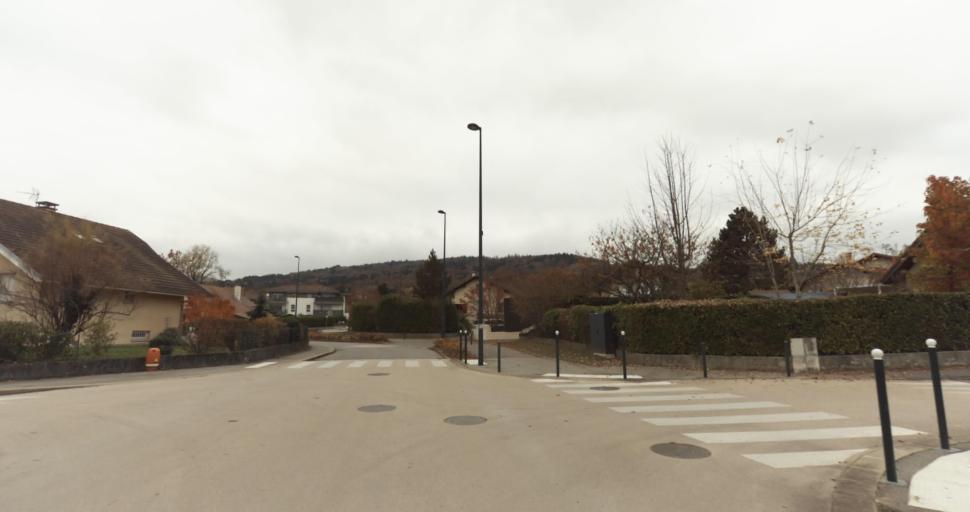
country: FR
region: Rhone-Alpes
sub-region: Departement de la Haute-Savoie
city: Metz-Tessy
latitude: 45.9506
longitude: 6.1098
